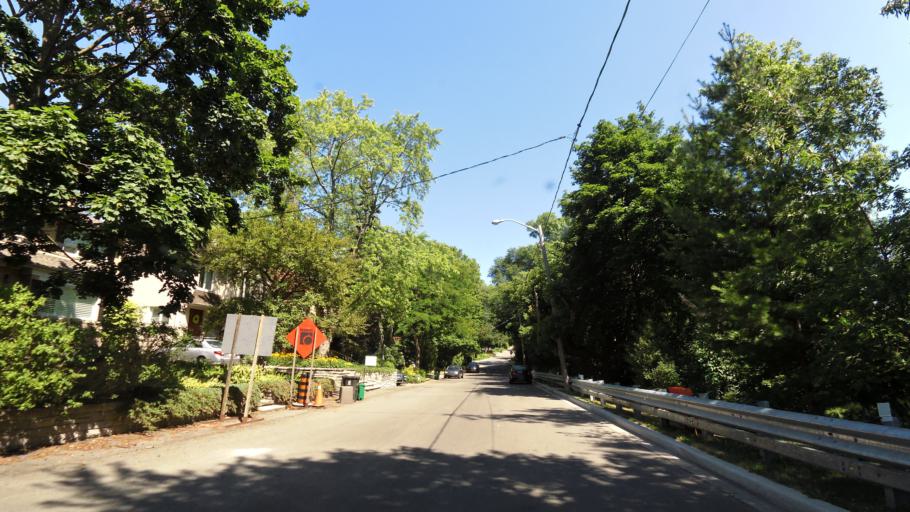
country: CA
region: Ontario
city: Etobicoke
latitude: 43.6536
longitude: -79.4930
